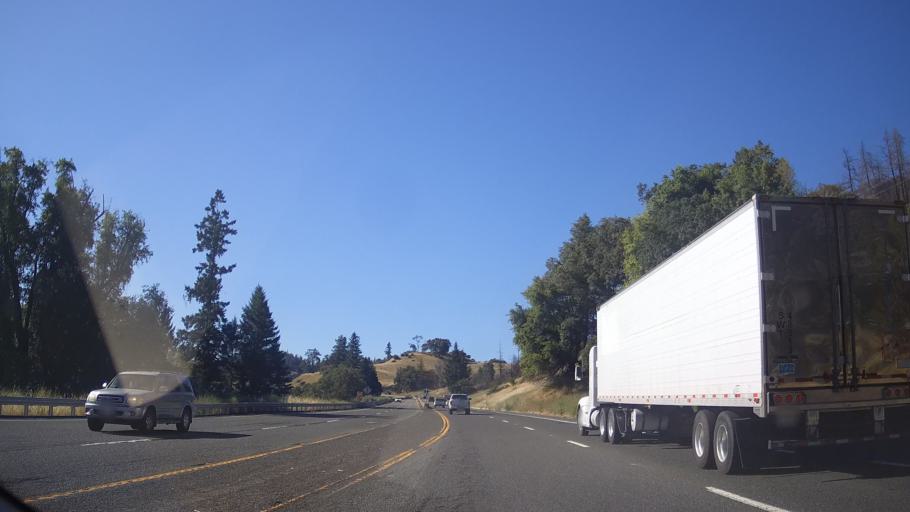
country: US
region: California
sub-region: Mendocino County
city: Willits
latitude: 39.3255
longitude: -123.3014
